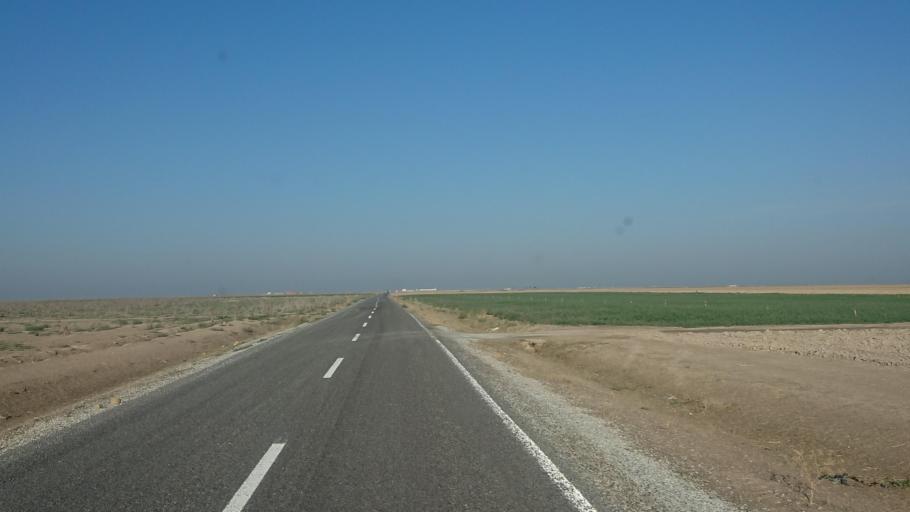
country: TR
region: Aksaray
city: Yesilova
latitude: 38.3878
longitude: 33.7684
